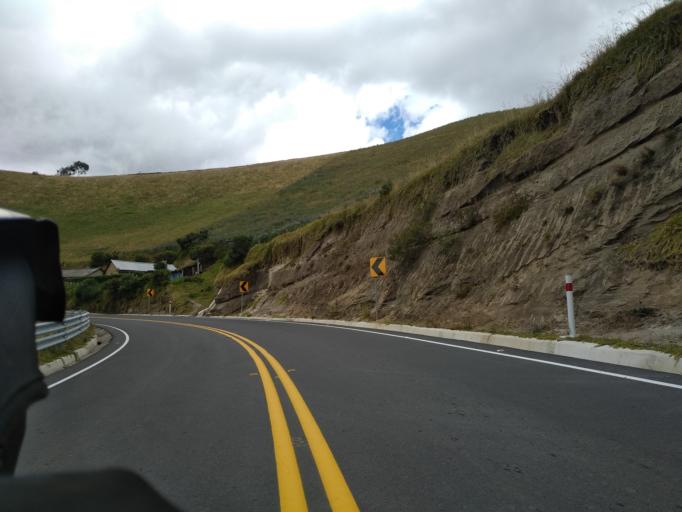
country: EC
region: Cotopaxi
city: Saquisili
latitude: -0.7817
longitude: -78.9119
